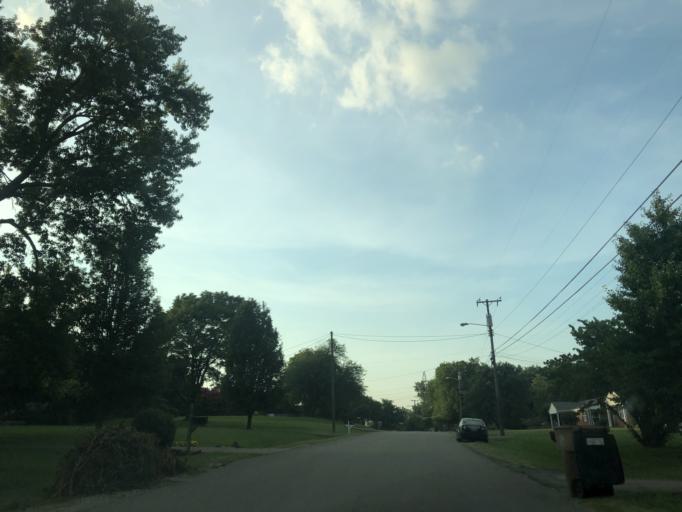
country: US
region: Tennessee
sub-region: Davidson County
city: Nashville
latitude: 36.1598
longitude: -86.7045
